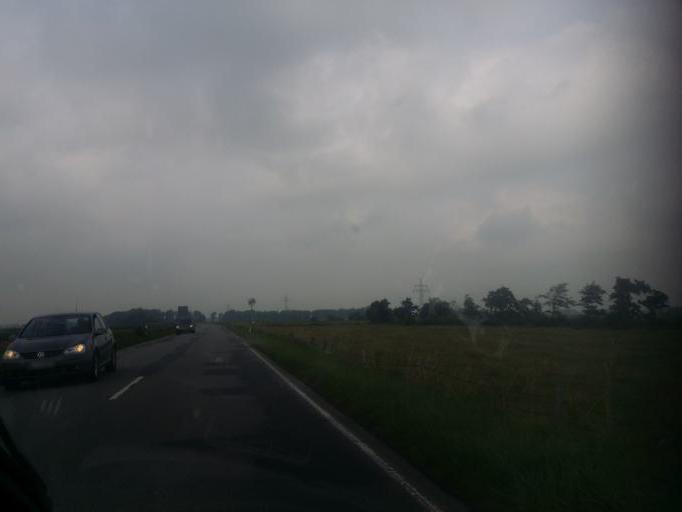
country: DE
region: Schleswig-Holstein
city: Kleve
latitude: 54.3085
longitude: 9.1100
